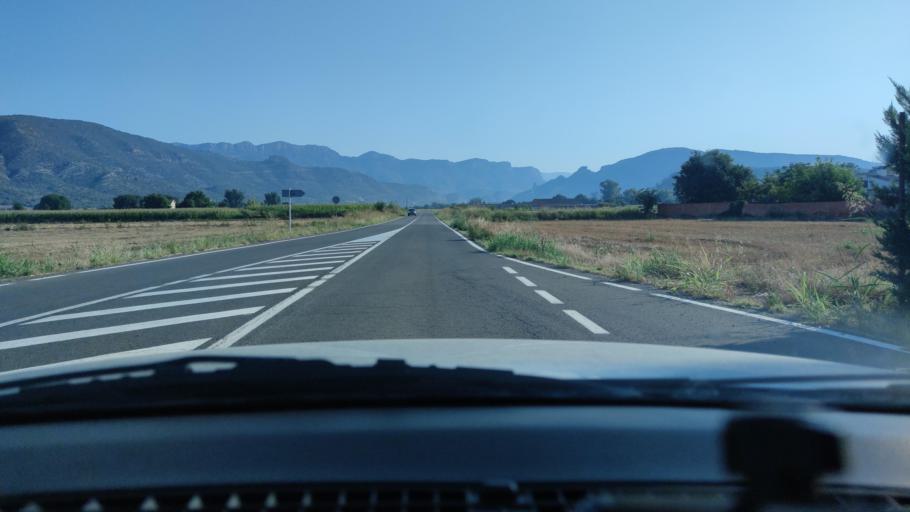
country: ES
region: Catalonia
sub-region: Provincia de Lleida
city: Balaguer
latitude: 41.8385
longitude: 0.8199
